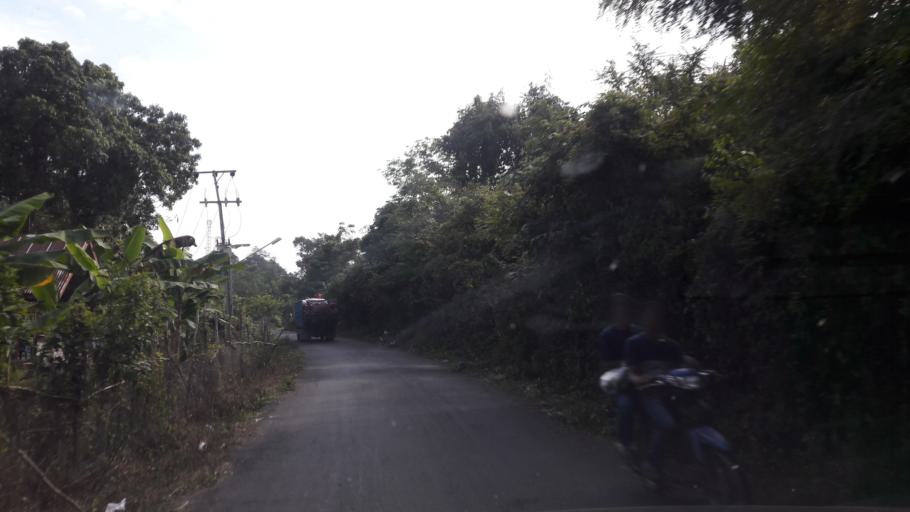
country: ID
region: South Sumatra
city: Gunungmenang
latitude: -3.1087
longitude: 103.9533
